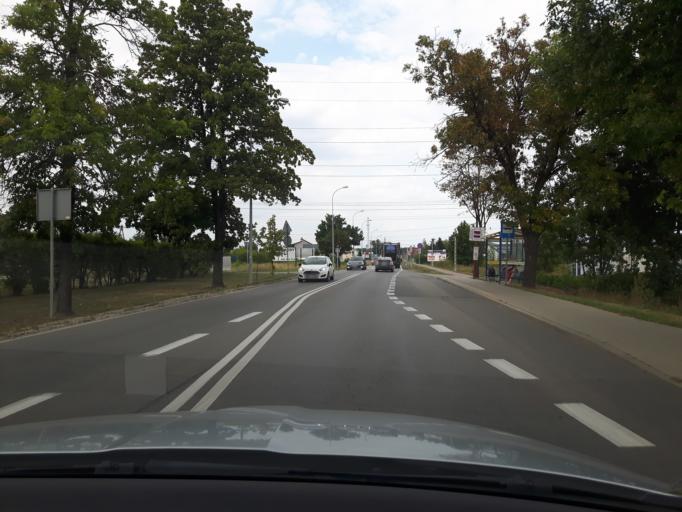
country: PL
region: Masovian Voivodeship
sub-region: Powiat legionowski
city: Stanislawow Pierwszy
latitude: 52.3705
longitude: 21.0289
